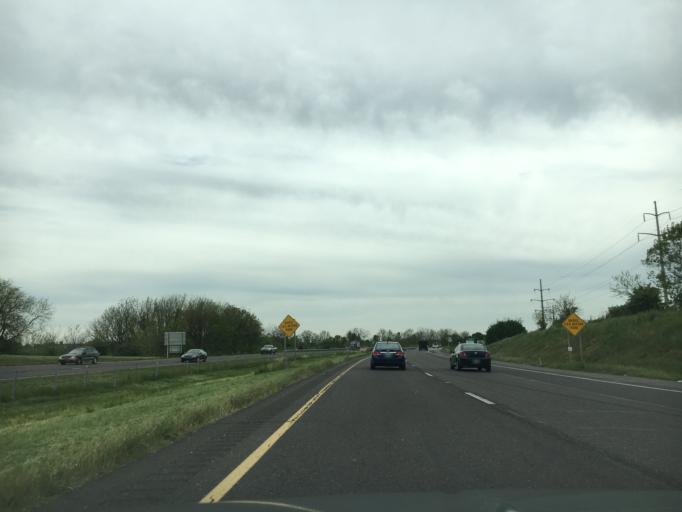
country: US
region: Pennsylvania
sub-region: Lancaster County
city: Ephrata
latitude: 40.1595
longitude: -76.1527
